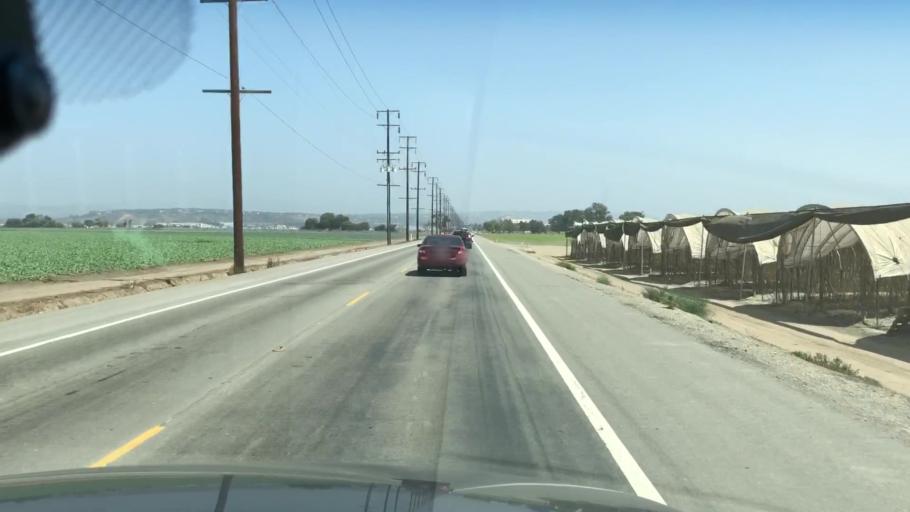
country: US
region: California
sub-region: Ventura County
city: Oxnard
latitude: 34.1884
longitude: -119.1122
